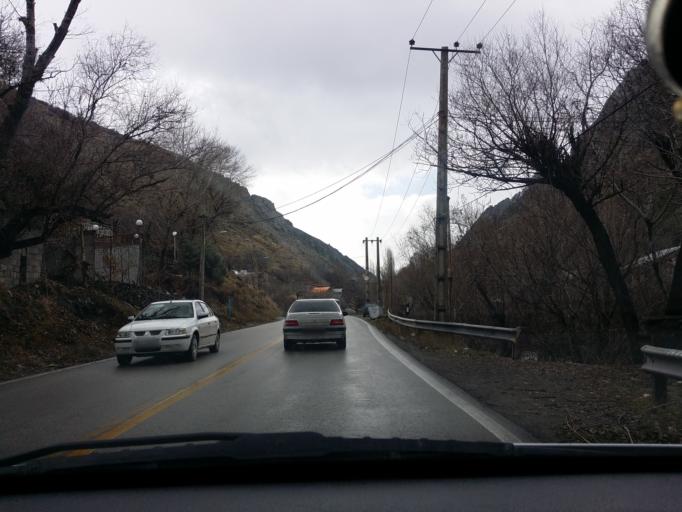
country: IR
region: Tehran
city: Tajrish
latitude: 36.0254
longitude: 51.2549
